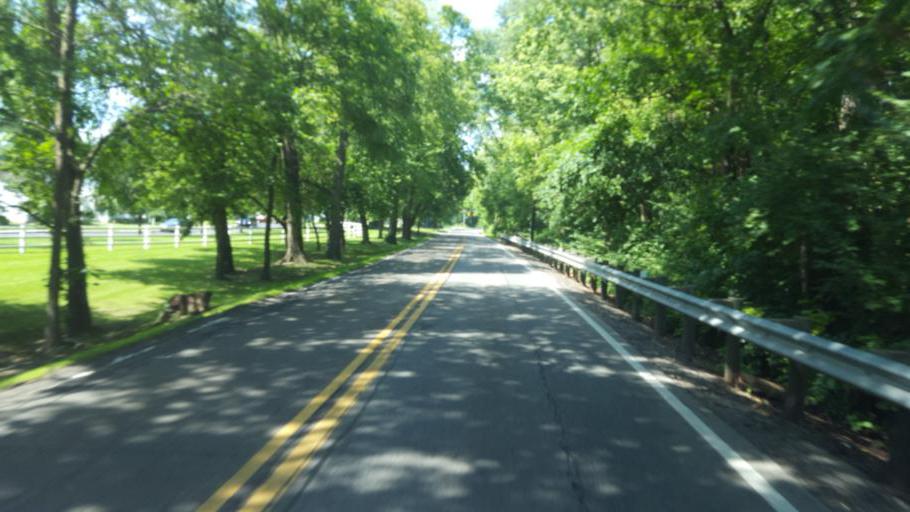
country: US
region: Ohio
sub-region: Franklin County
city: Bexley
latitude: 40.0073
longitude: -82.9352
